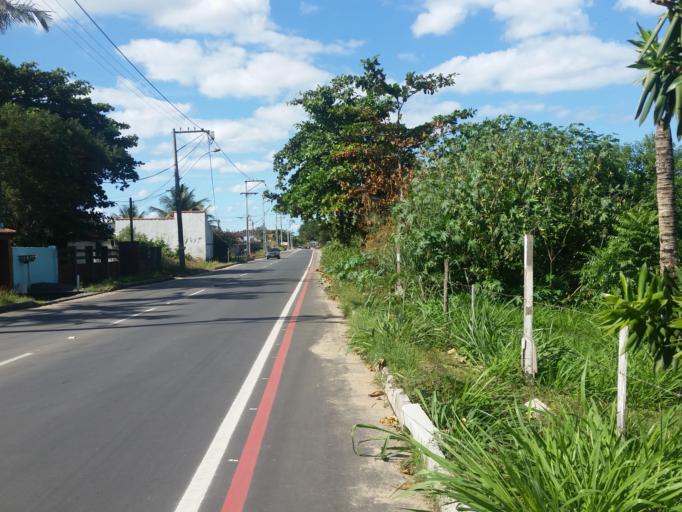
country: BR
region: Rio de Janeiro
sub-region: Marica
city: Marica
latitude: -22.9680
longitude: -42.9640
